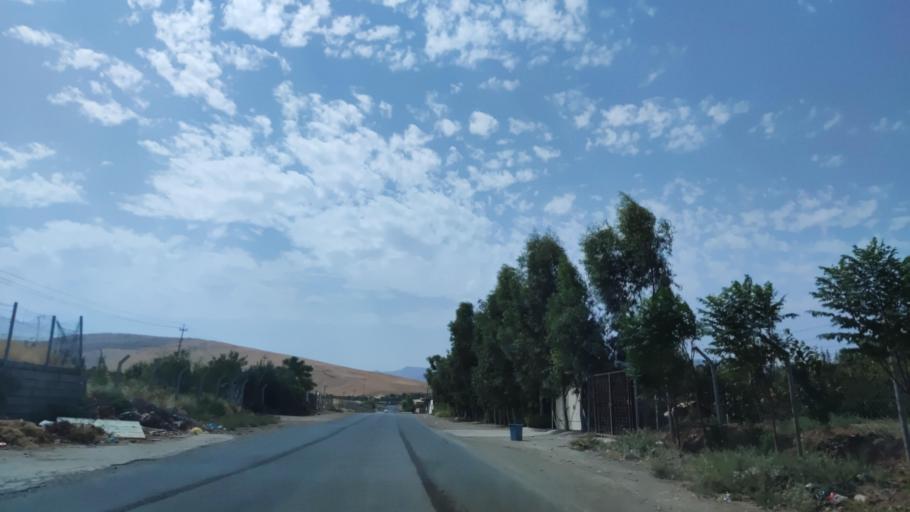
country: IQ
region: Arbil
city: Shaqlawah
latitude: 36.4769
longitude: 44.3977
